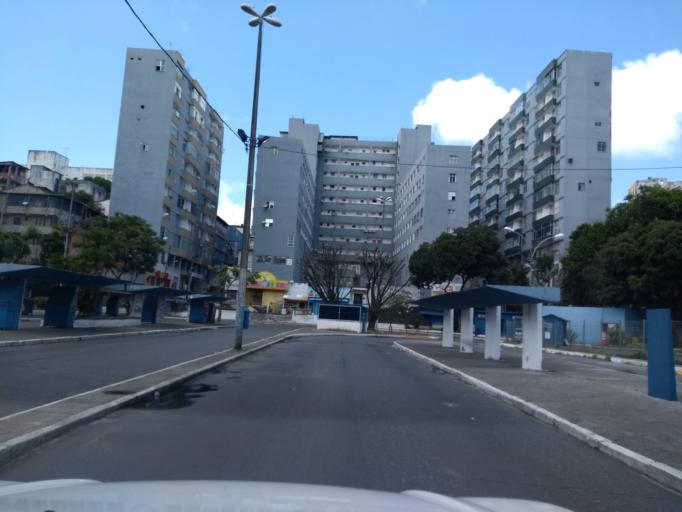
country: BR
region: Bahia
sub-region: Salvador
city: Salvador
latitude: -12.9785
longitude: -38.5126
